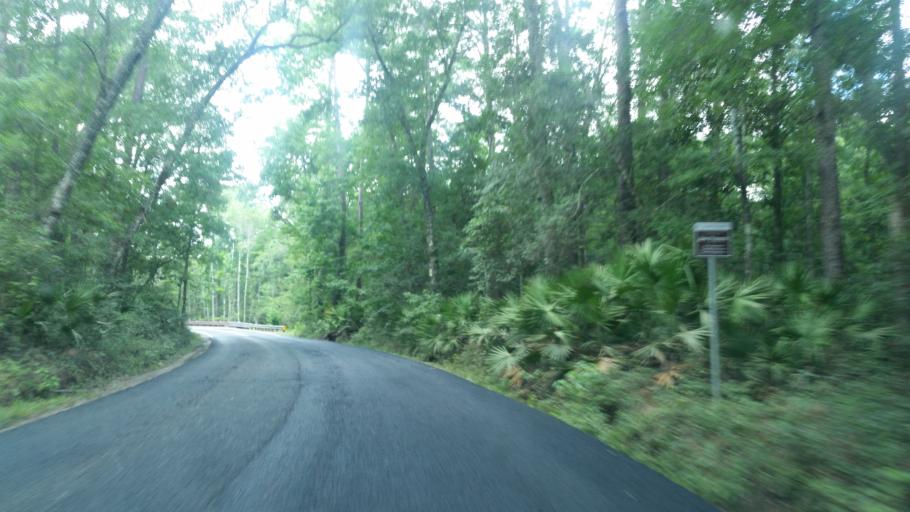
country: US
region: Florida
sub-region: Leon County
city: Woodville
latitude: 30.2859
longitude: -84.1479
